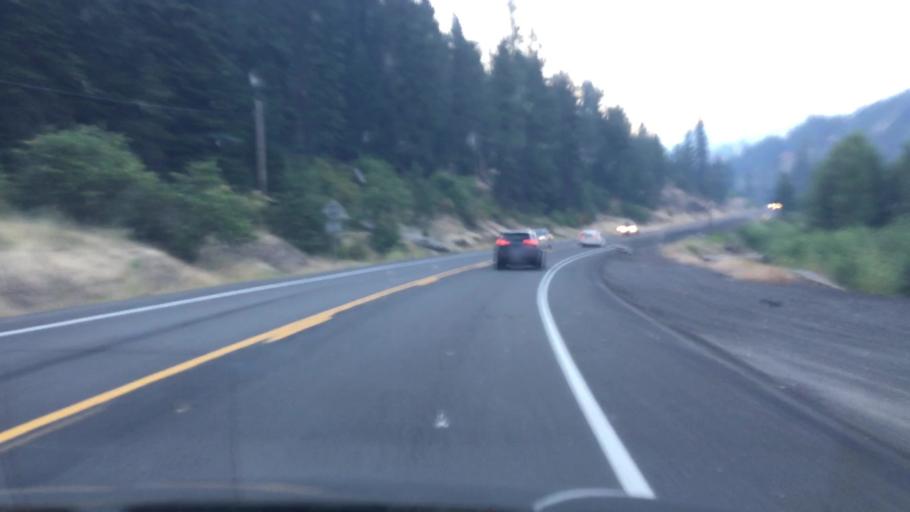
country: US
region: Idaho
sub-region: Valley County
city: McCall
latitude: 45.2051
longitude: -116.3128
